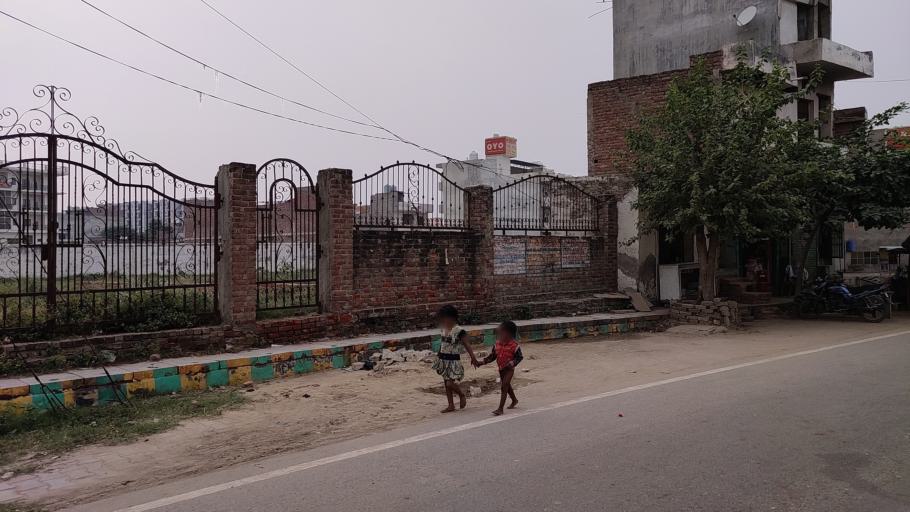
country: IN
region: Uttar Pradesh
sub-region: Mathura
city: Vrindavan
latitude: 27.5662
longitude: 77.6759
